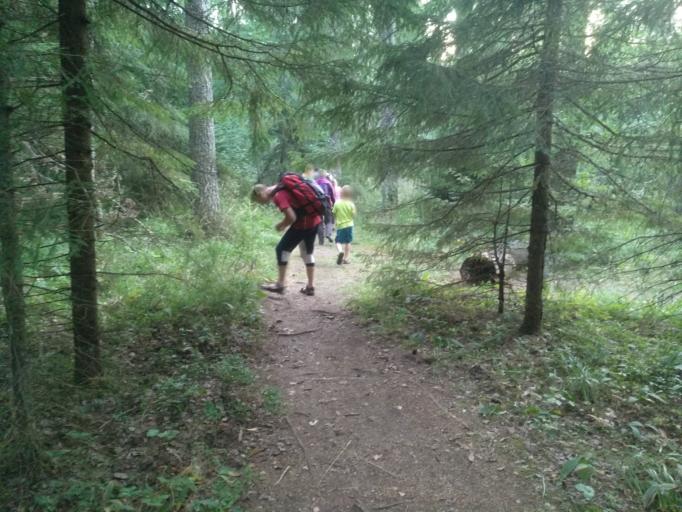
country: RU
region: Leningrad
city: Kuznechnoye
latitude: 61.1629
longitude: 29.7148
